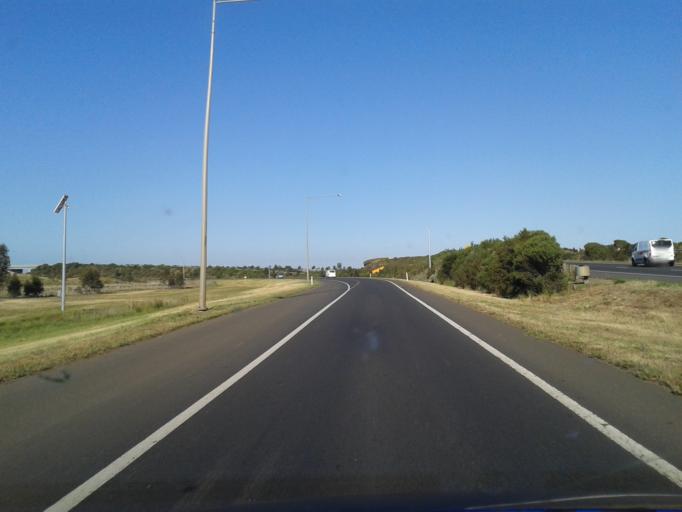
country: AU
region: Victoria
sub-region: Brimbank
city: Derrimut
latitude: -37.7990
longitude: 144.7808
